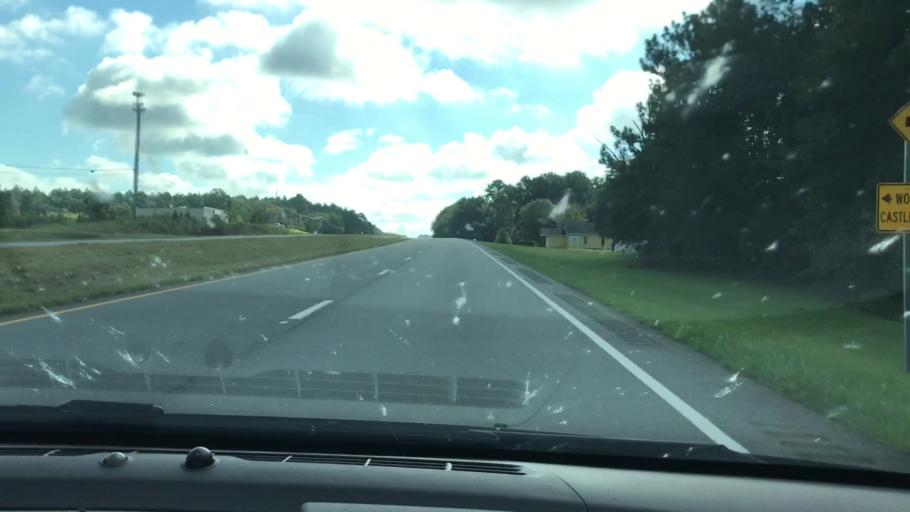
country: US
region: Georgia
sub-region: Worth County
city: Sylvester
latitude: 31.5520
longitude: -83.9399
